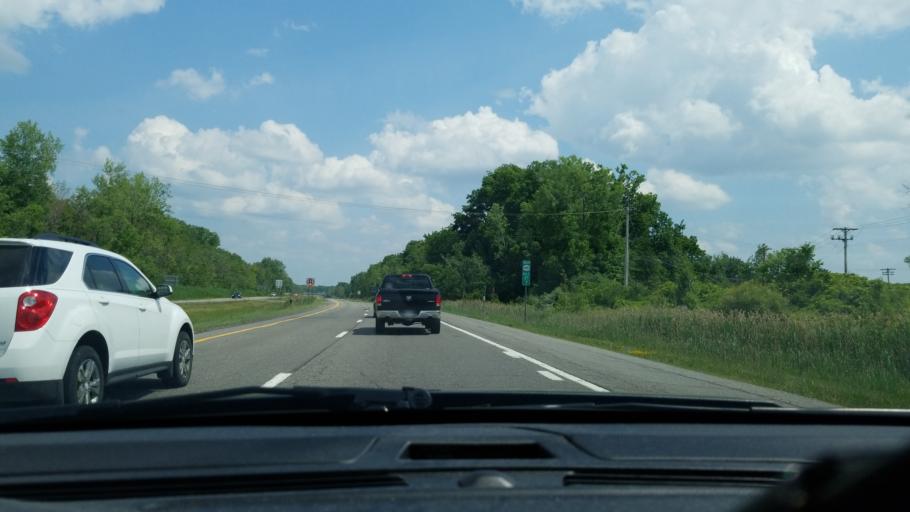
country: US
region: New York
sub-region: Onondaga County
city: Liverpool
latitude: 43.1814
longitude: -76.2276
